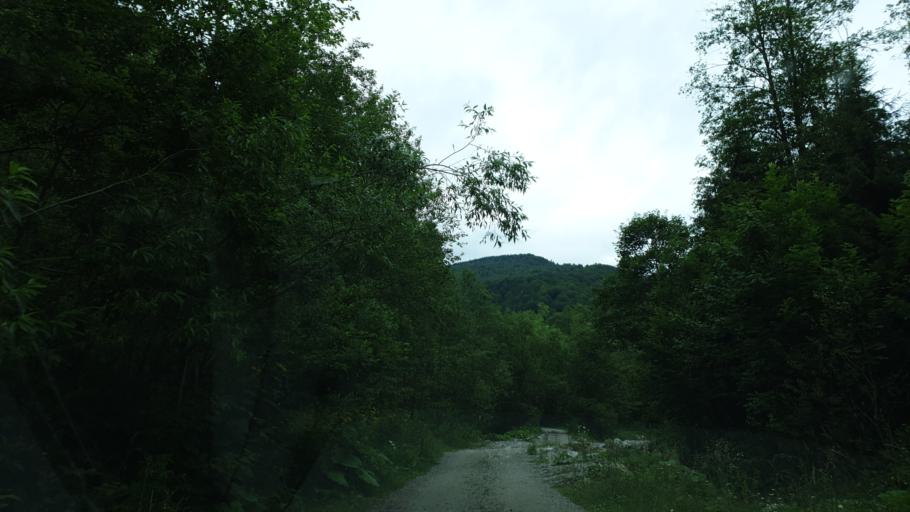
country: RO
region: Hunedoara
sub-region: Comuna Uricani
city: Uricani
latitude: 45.3058
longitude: 22.9866
